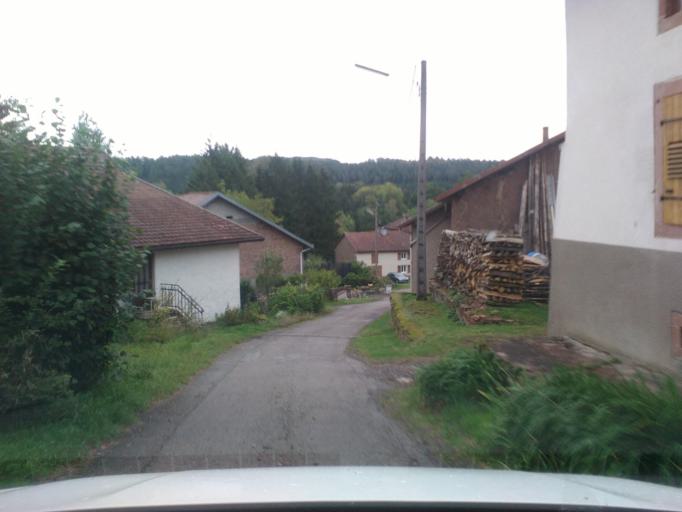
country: FR
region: Lorraine
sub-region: Departement des Vosges
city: Senones
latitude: 48.4107
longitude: 7.0273
